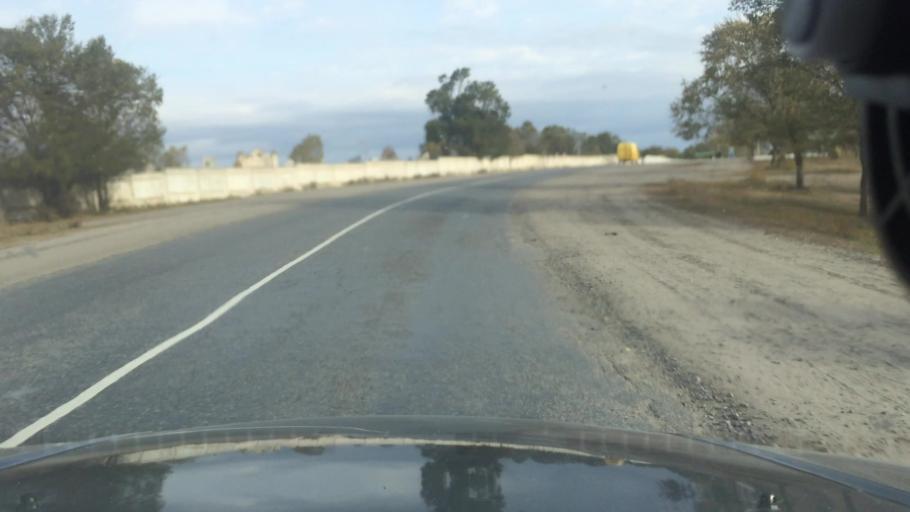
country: KG
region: Ysyk-Koel
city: Karakol
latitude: 42.5365
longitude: 78.3820
